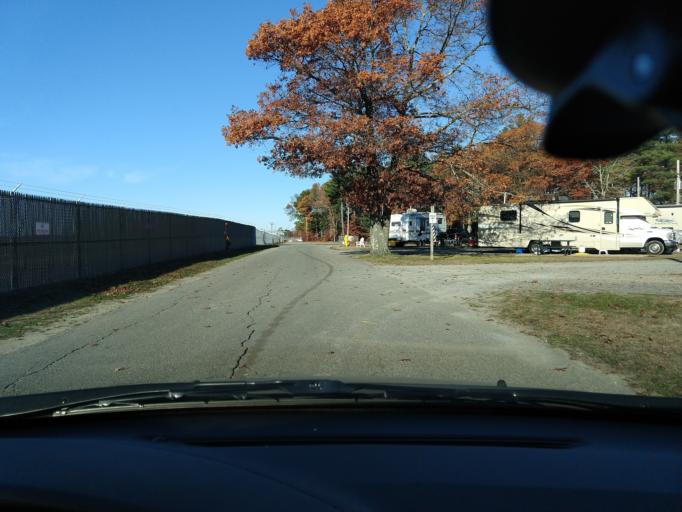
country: US
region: Massachusetts
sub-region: Middlesex County
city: Bedford
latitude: 42.4722
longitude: -71.2800
